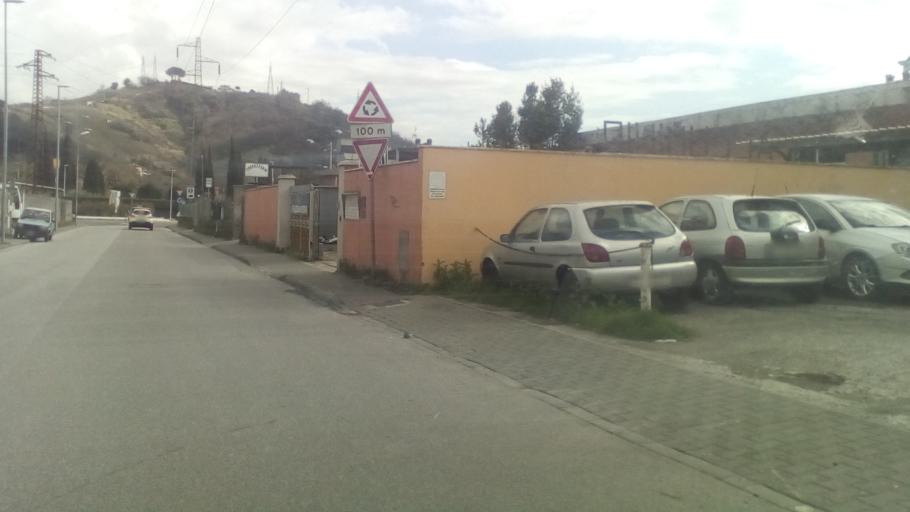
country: IT
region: Tuscany
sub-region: Provincia di Massa-Carrara
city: Carrara
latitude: 44.0566
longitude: 10.0742
